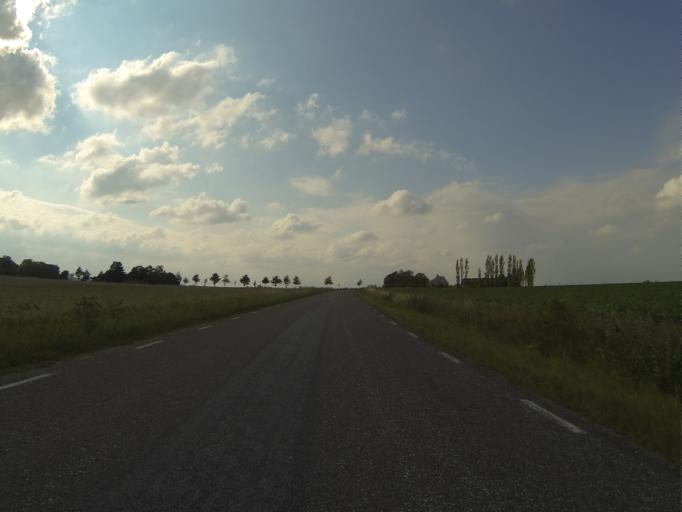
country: SE
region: Skane
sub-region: Lunds Kommun
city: Lund
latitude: 55.7493
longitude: 13.2356
